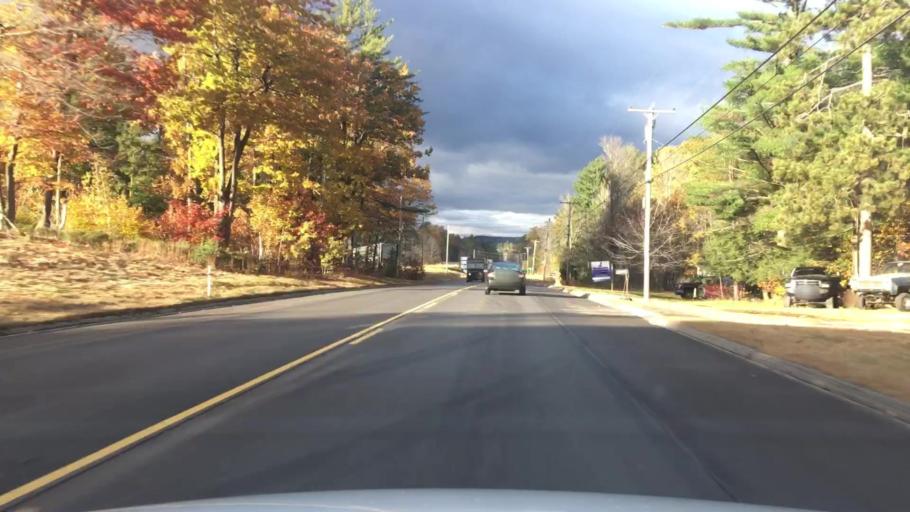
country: US
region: Maine
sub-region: Androscoggin County
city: Livermore
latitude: 44.3691
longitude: -70.2511
